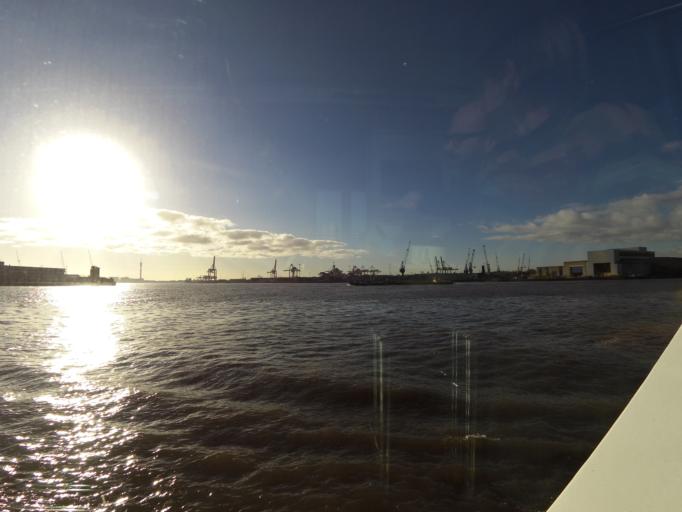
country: NL
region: South Holland
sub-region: Gemeente Rotterdam
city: Delfshaven
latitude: 51.9030
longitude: 4.4364
